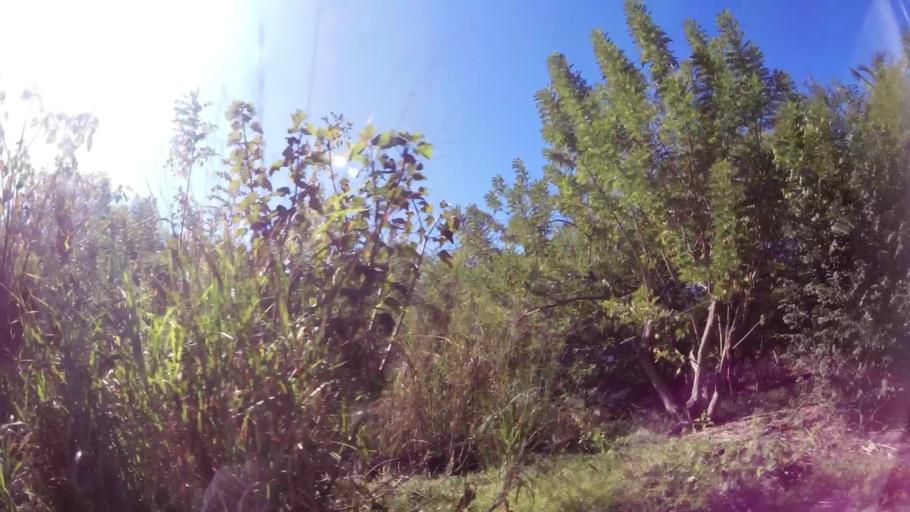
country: GT
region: Santa Rosa
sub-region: Municipio de Taxisco
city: Taxisco
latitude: 13.8691
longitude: -90.4186
